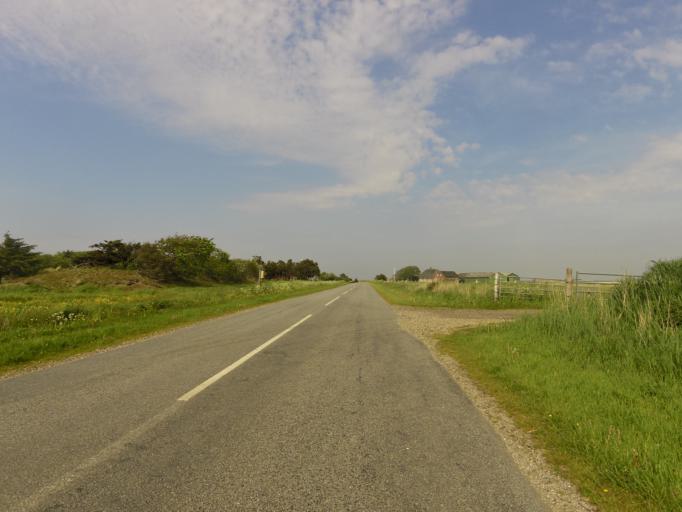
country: DE
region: Schleswig-Holstein
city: List
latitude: 55.1790
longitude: 8.5573
